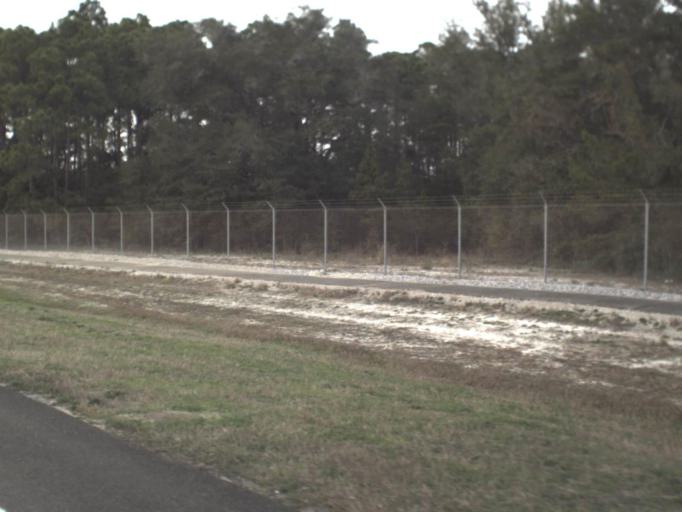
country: US
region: Florida
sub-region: Bay County
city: Tyndall Air Force Base
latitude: 30.0767
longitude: -85.5986
